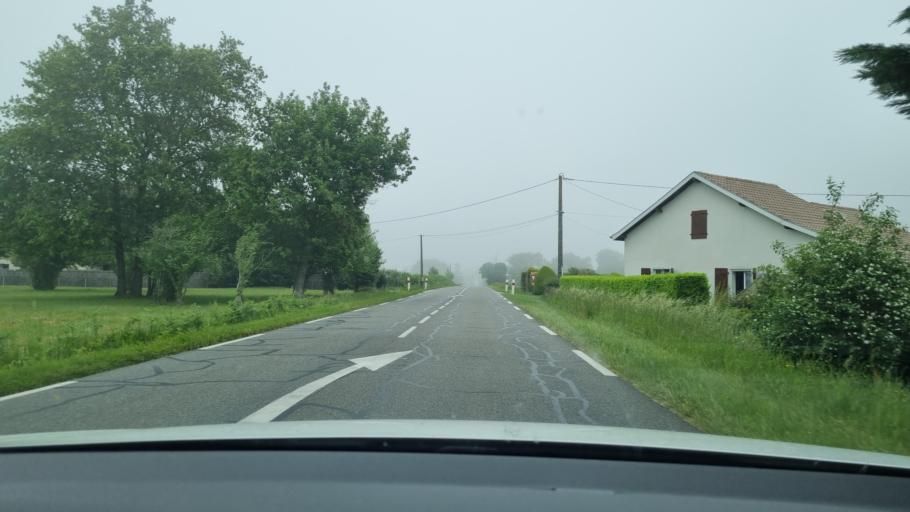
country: FR
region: Aquitaine
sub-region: Departement des Landes
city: Amou
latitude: 43.5333
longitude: -0.6941
